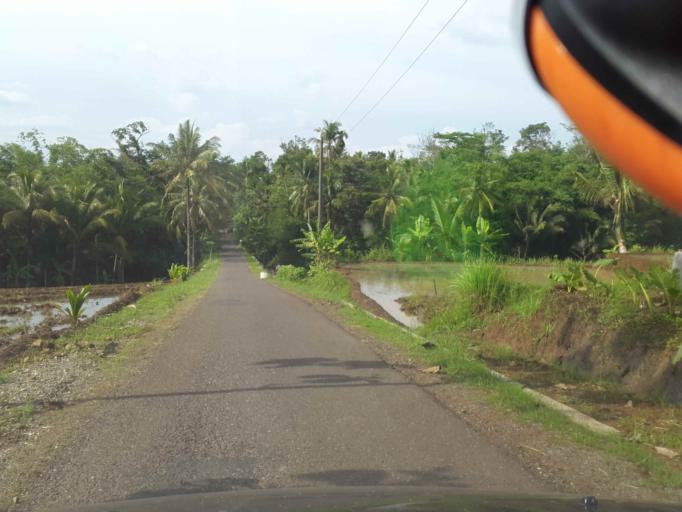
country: ID
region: Central Java
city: Gombong
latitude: -7.4706
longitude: 109.4887
